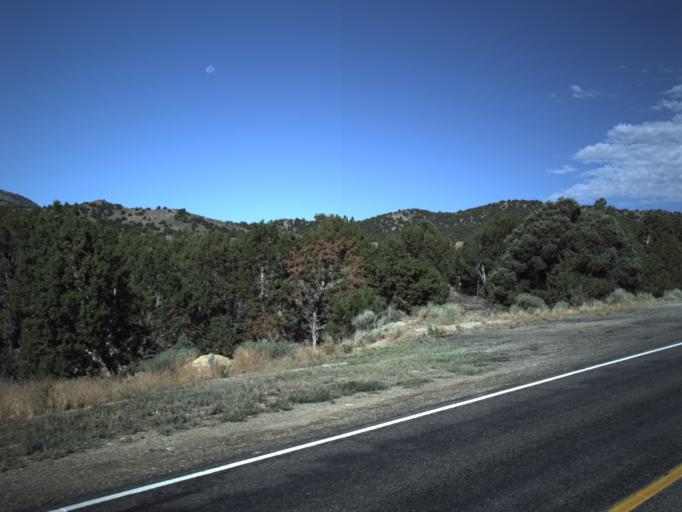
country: US
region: Utah
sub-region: Utah County
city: Genola
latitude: 39.9675
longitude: -112.0527
